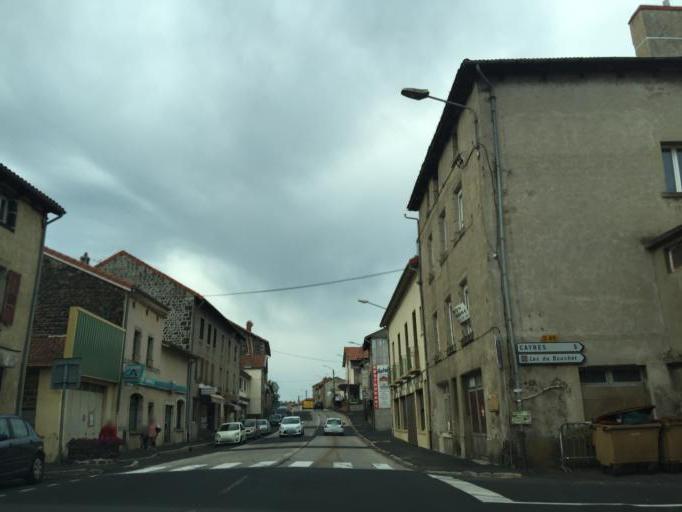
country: FR
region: Auvergne
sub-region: Departement de la Haute-Loire
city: Solignac-sur-Loire
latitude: 44.8934
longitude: 3.8492
